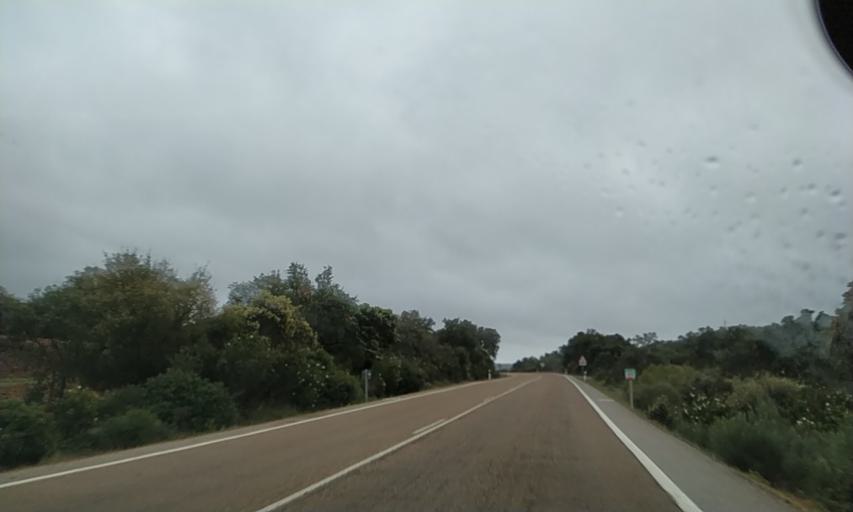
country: ES
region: Extremadura
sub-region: Provincia de Badajoz
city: Puebla de Obando
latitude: 39.2833
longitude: -6.5218
